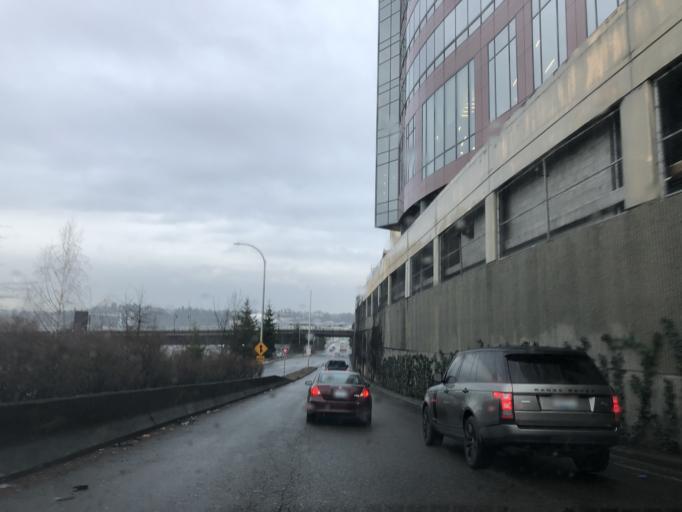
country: US
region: Washington
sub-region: Pierce County
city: Tacoma
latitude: 47.2552
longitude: -122.4370
